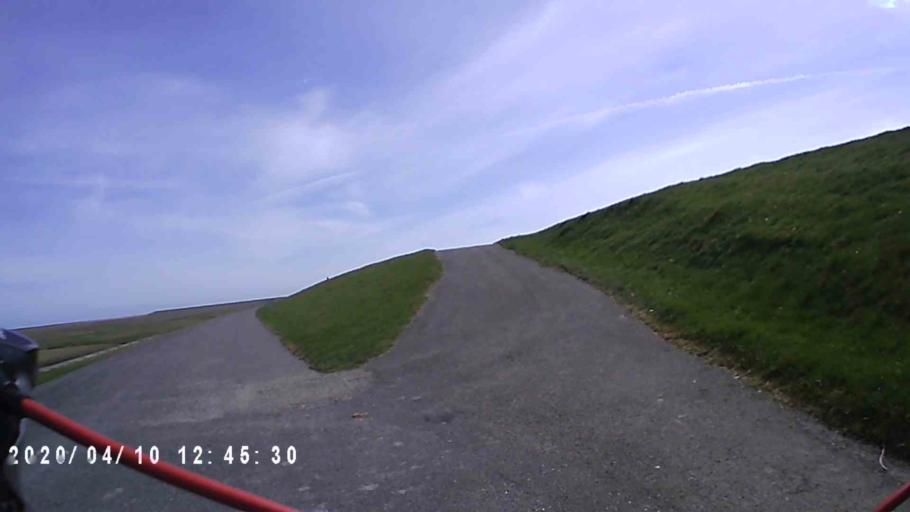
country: NL
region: Groningen
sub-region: Gemeente De Marne
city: Ulrum
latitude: 53.4173
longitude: 6.4183
